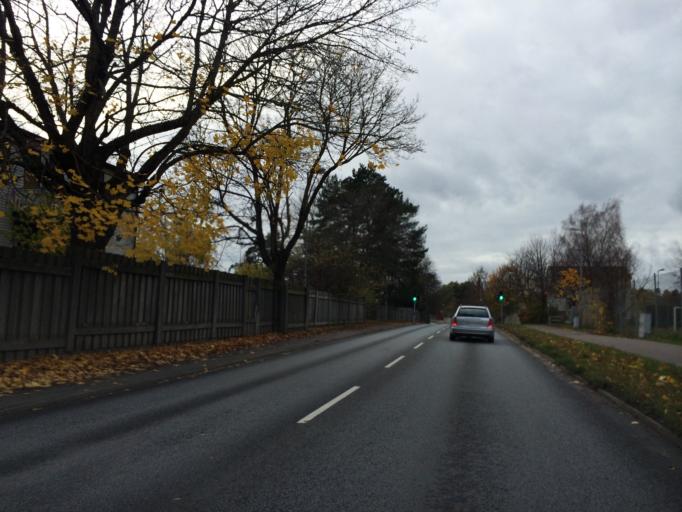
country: SE
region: Stockholm
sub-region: Sollentuna Kommun
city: Sollentuna
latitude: 59.4599
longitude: 17.9185
